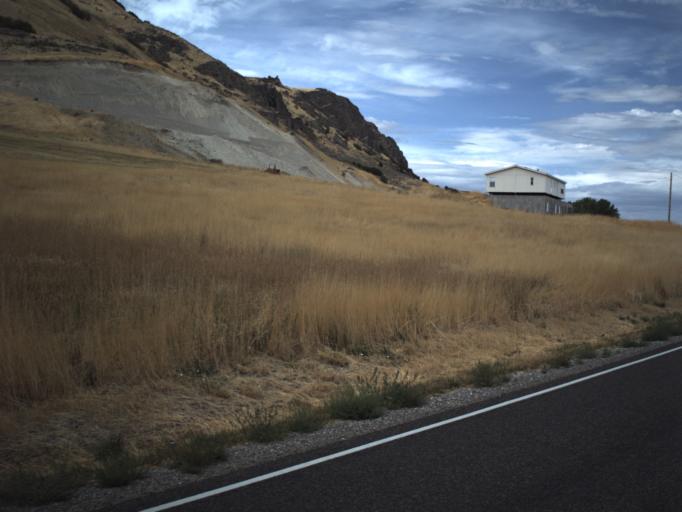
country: US
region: Utah
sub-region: Cache County
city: Benson
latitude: 41.8927
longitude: -111.9492
